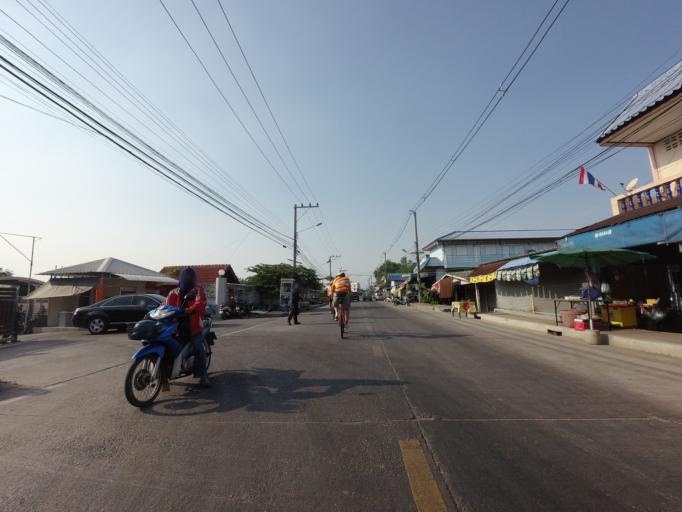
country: TH
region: Samut Sakhon
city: Samut Sakhon
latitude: 13.5271
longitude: 100.2706
